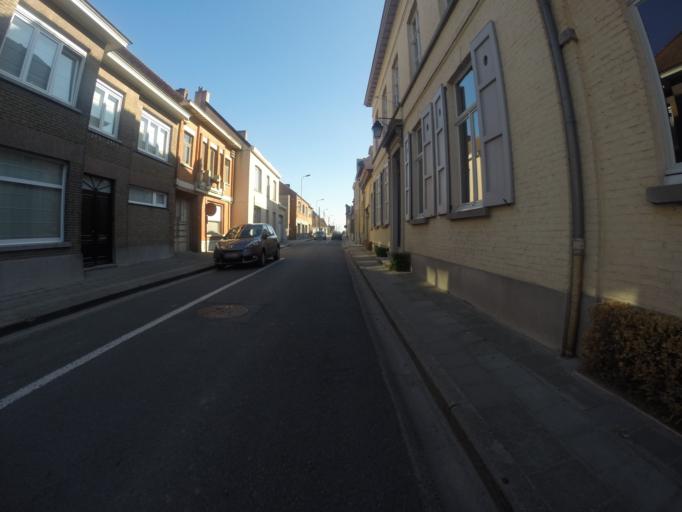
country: BE
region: Flanders
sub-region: Provincie West-Vlaanderen
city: Dentergem
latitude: 50.9950
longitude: 3.4219
